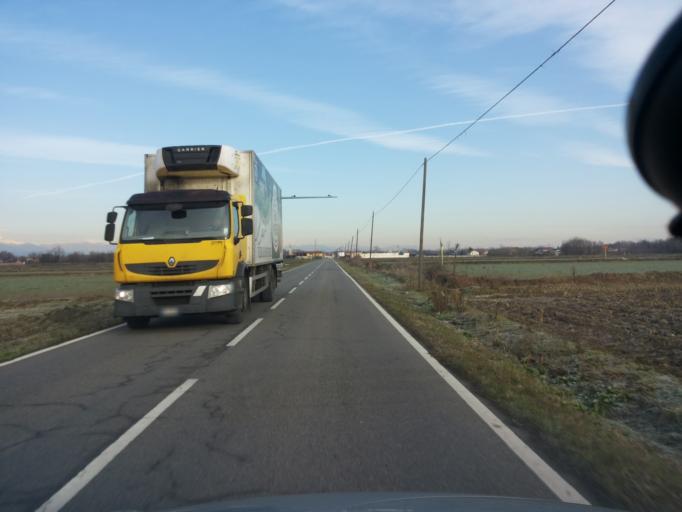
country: IT
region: Piedmont
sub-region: Provincia di Vercelli
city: Greggio
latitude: 45.4435
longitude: 8.3838
